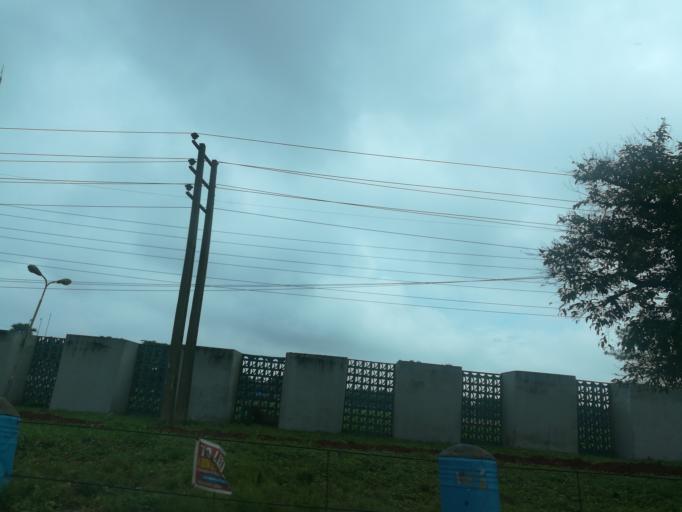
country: NG
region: Lagos
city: Ikorodu
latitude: 6.6481
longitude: 3.5180
